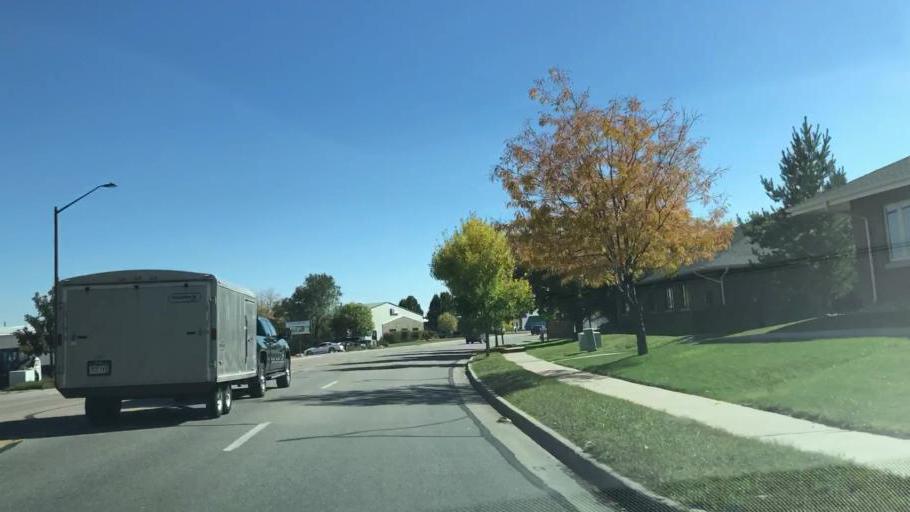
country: US
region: Colorado
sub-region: Larimer County
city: Fort Collins
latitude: 40.5721
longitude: -105.0468
